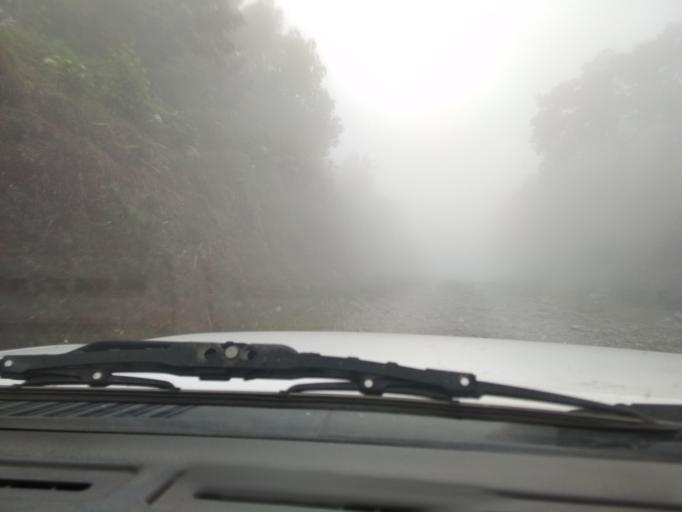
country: MX
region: Veracruz
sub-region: La Perla
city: Barrio de San Miguel
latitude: 18.9485
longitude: -97.1217
